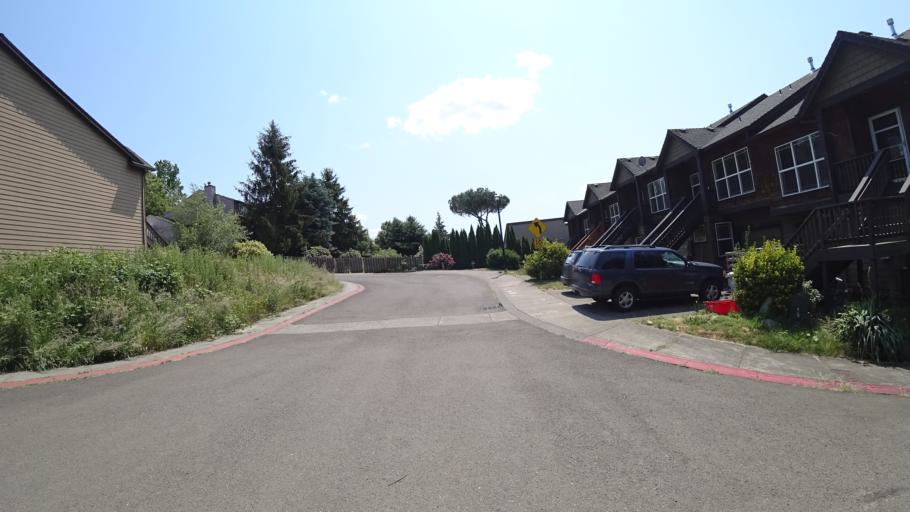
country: US
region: Oregon
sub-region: Multnomah County
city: Lents
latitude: 45.4528
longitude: -122.5710
